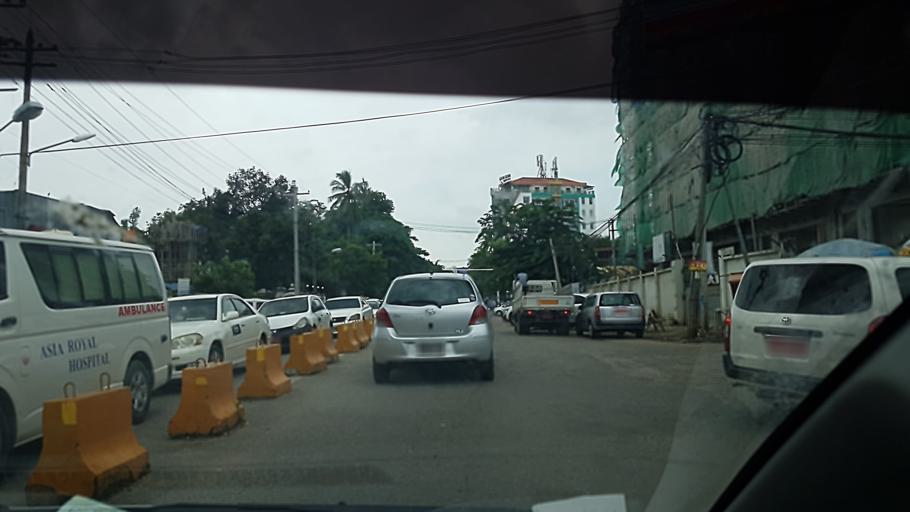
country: MM
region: Yangon
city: Yangon
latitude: 16.7981
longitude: 96.1309
